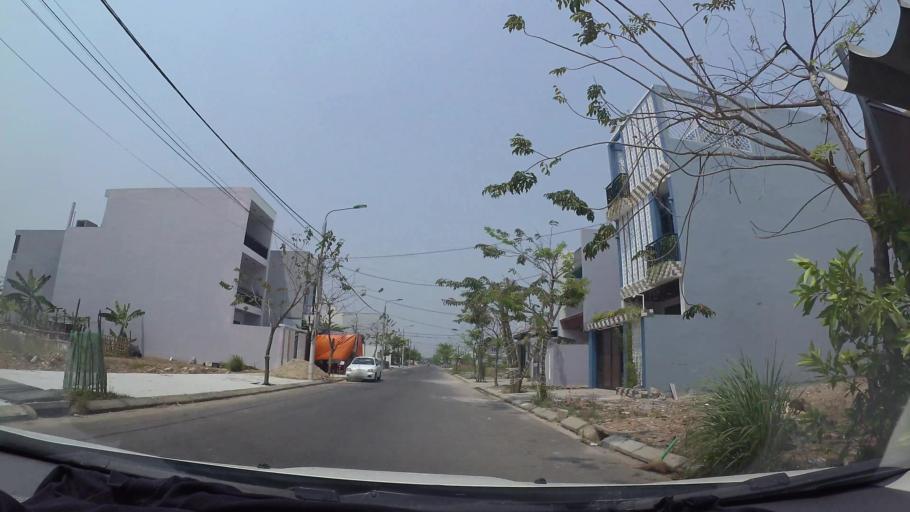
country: VN
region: Da Nang
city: Cam Le
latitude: 16.0165
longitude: 108.2215
